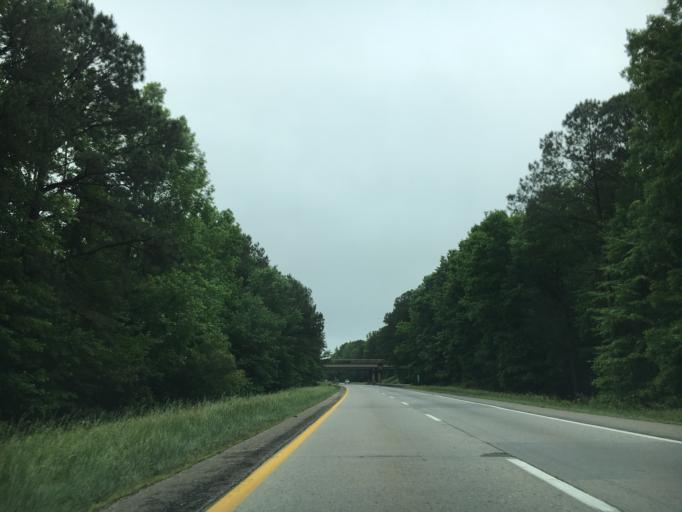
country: US
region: Virginia
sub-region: Chesterfield County
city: Matoaca
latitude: 37.1882
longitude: -77.4901
